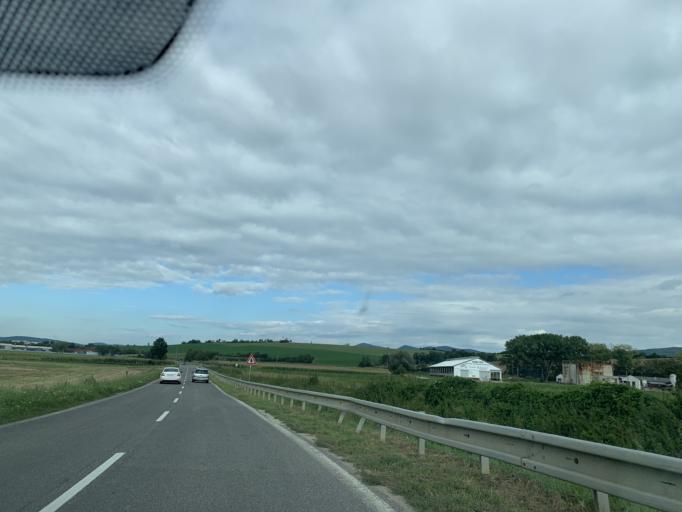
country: SK
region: Trenciansky
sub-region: Okres Trencin
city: Trencin
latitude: 48.8280
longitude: 17.9659
